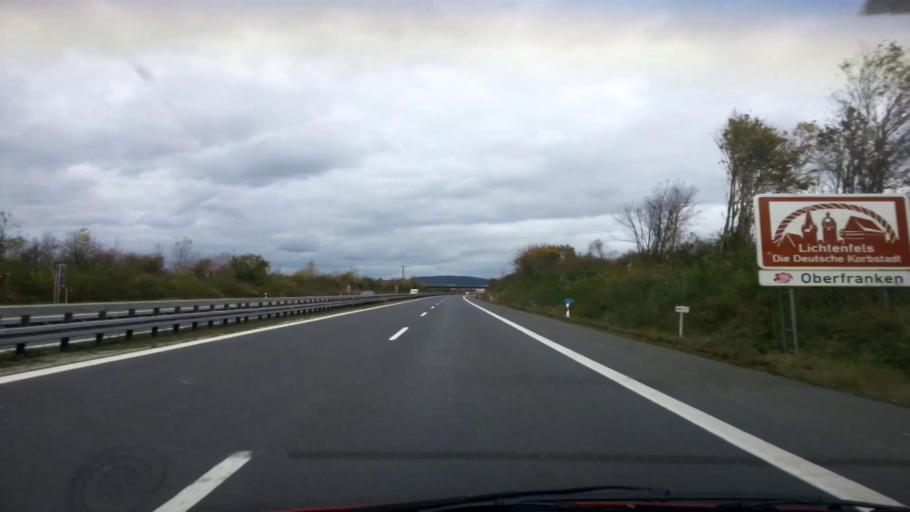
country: DE
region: Bavaria
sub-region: Upper Franconia
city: Bad Staffelstein
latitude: 50.1120
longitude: 11.0159
